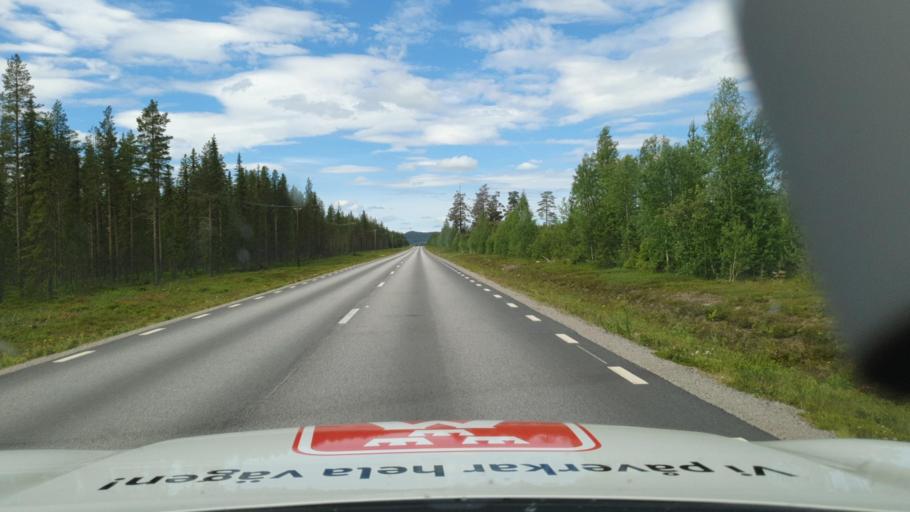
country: SE
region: Vaesterbotten
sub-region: Norsjo Kommun
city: Norsjoe
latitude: 65.2393
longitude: 19.7172
